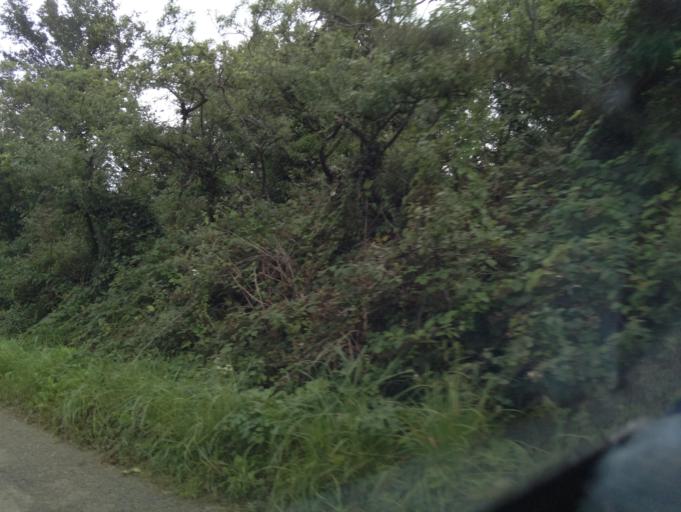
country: GB
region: England
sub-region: Somerset
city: Evercreech
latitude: 51.1814
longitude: -2.5067
